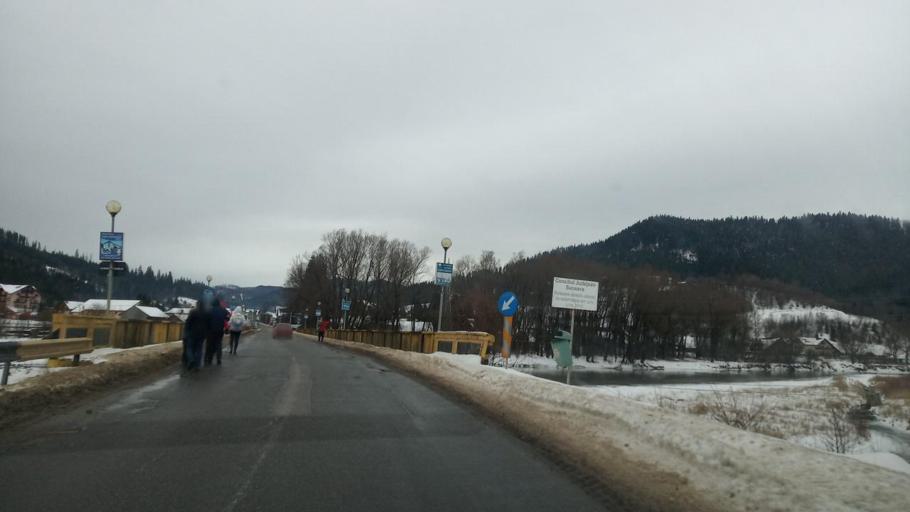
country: RO
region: Suceava
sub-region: Oras Gura Humorului
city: Gura Humorului
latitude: 47.5401
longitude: 25.8643
